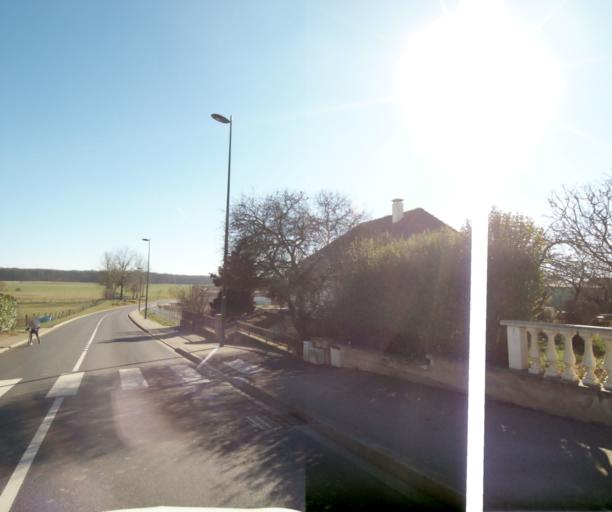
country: FR
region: Lorraine
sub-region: Departement de Meurthe-et-Moselle
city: Saulxures-les-Nancy
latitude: 48.6866
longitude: 6.2452
